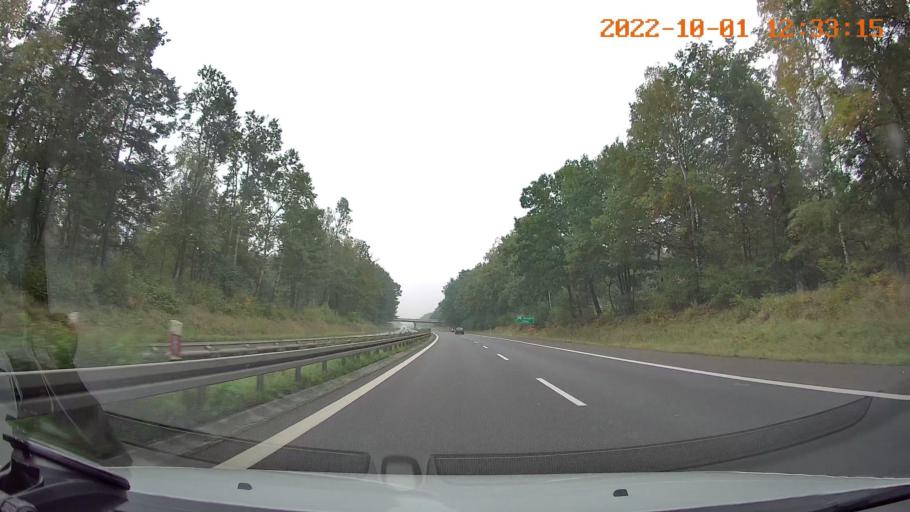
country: PL
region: Silesian Voivodeship
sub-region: Powiat bierunsko-ledzinski
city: Ledziny
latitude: 50.1525
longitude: 19.1171
